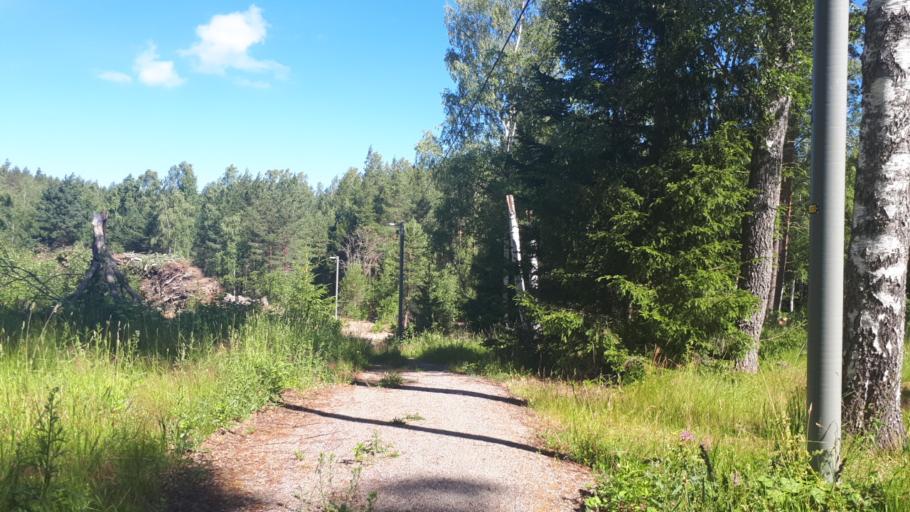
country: SE
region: Soedermanland
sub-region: Katrineholms Kommun
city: Katrineholm
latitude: 59.0983
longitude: 16.1940
